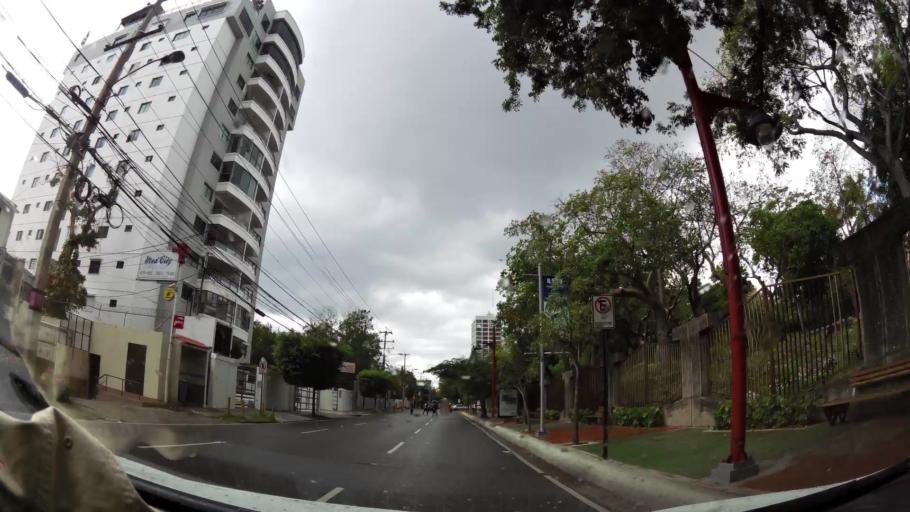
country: DO
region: Nacional
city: La Julia
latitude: 18.4653
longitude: -69.9194
